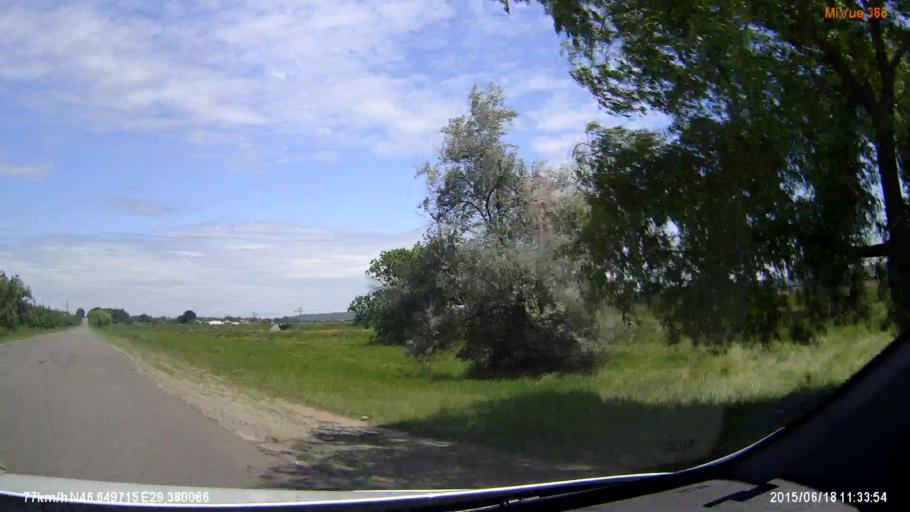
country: MD
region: Causeni
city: Causeni
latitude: 46.6494
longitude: 29.3798
